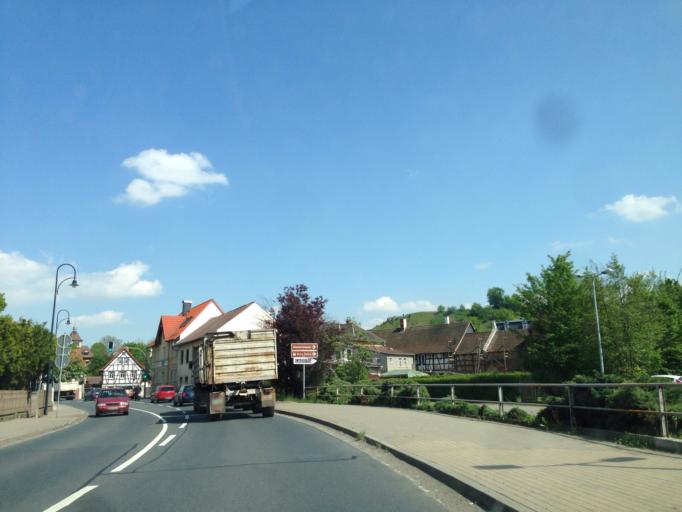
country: DE
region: Thuringia
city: Krolpa
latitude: 50.6769
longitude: 11.5382
